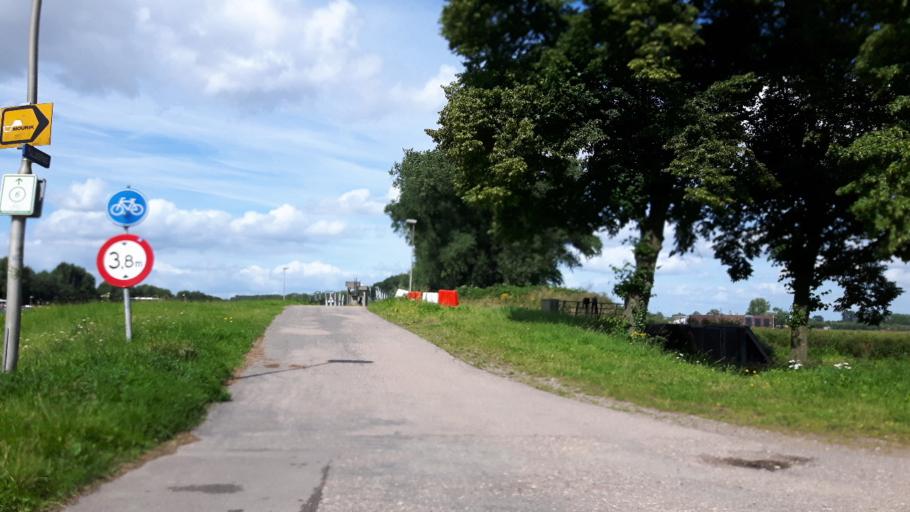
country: NL
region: Utrecht
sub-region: Gemeente Nieuwegein
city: Nieuwegein
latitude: 52.0209
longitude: 5.1139
